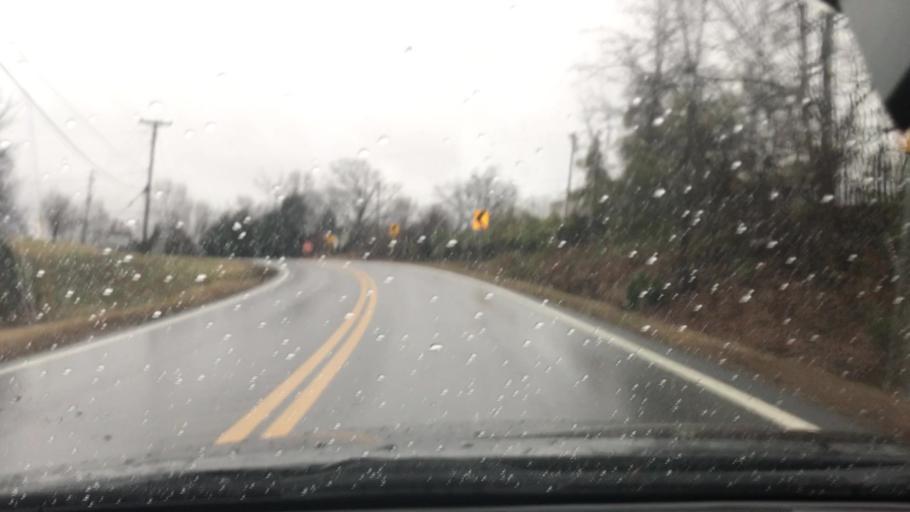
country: US
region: Tennessee
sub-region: Cheatham County
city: Ashland City
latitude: 36.2762
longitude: -87.1195
